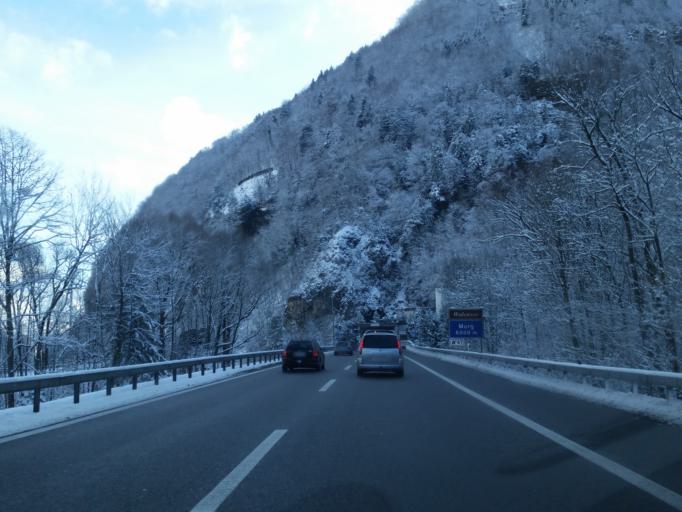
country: CH
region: Saint Gallen
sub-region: Wahlkreis See-Gaster
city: Weesen
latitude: 47.1256
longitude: 9.1122
